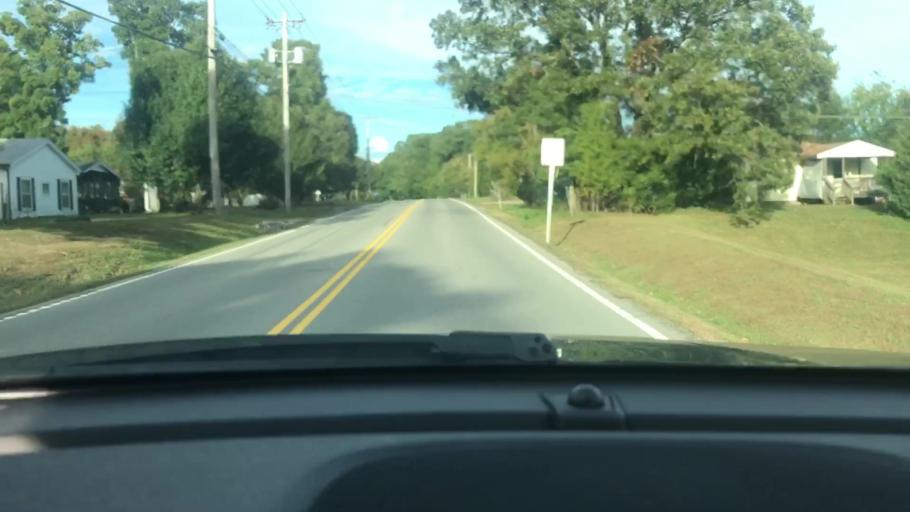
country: US
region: Tennessee
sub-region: Dickson County
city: White Bluff
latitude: 36.1393
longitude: -87.2384
